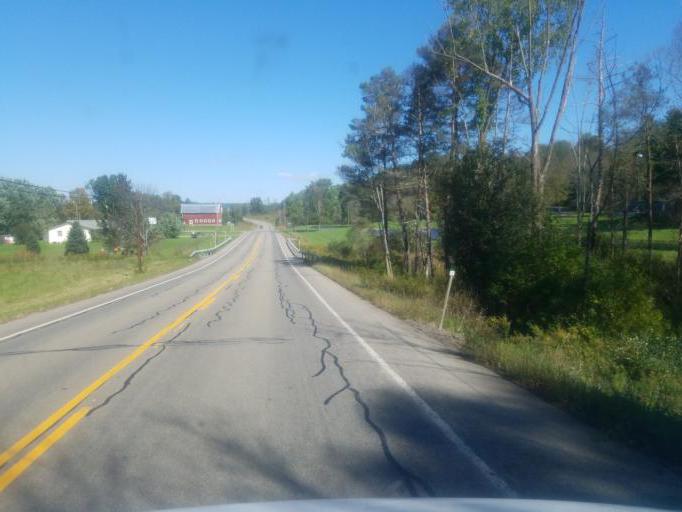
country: US
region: New York
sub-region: Allegany County
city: Friendship
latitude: 42.3132
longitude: -78.1318
